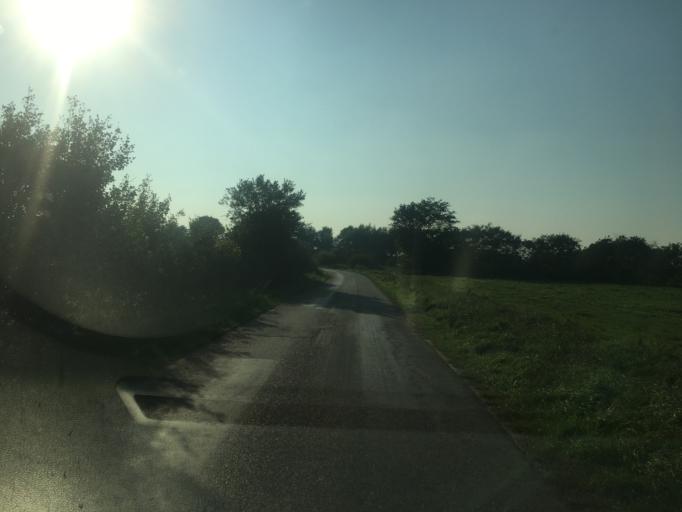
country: DE
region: Schleswig-Holstein
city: Bramstedtlund
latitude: 54.9639
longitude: 9.0609
